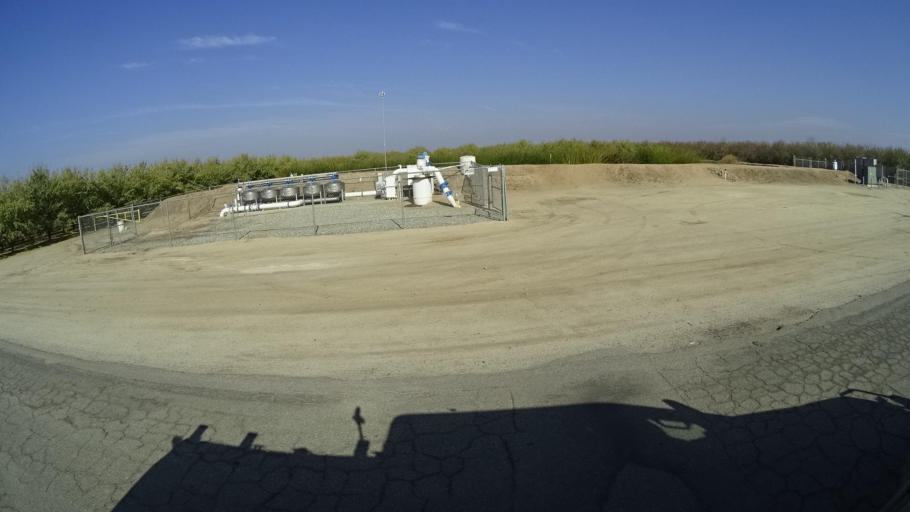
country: US
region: California
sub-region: Kern County
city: McFarland
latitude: 35.6891
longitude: -119.1610
